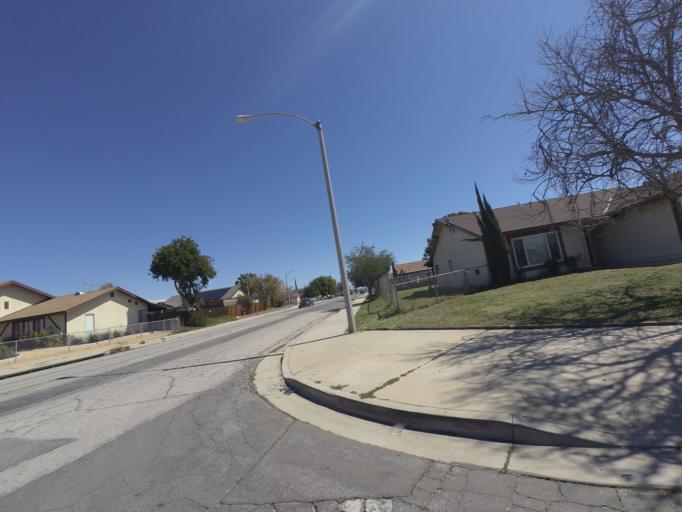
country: US
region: California
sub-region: Riverside County
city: Moreno Valley
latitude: 33.9136
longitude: -117.2377
